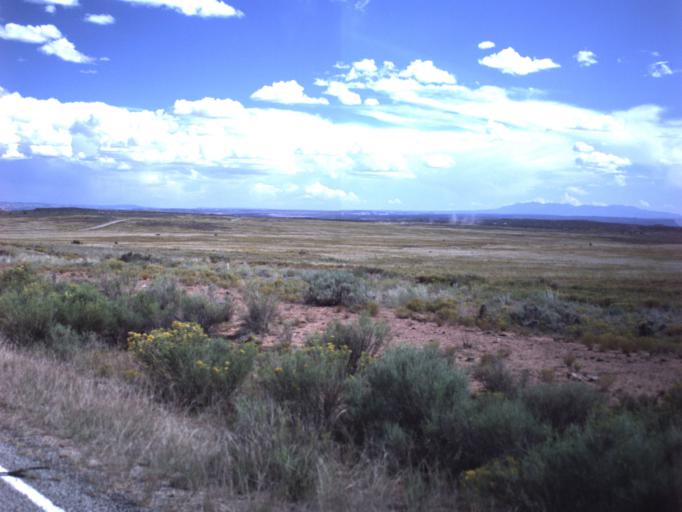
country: US
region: Utah
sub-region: Grand County
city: Moab
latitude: 38.5453
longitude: -109.7656
